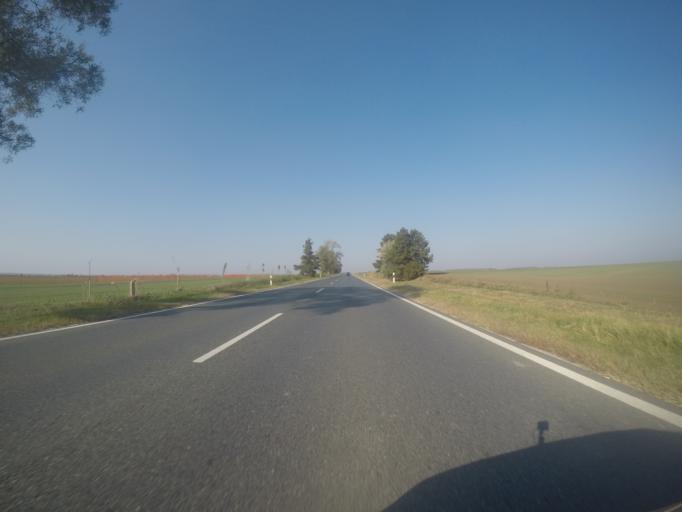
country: HU
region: Tolna
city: Madocsa
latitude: 46.7152
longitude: 18.8866
